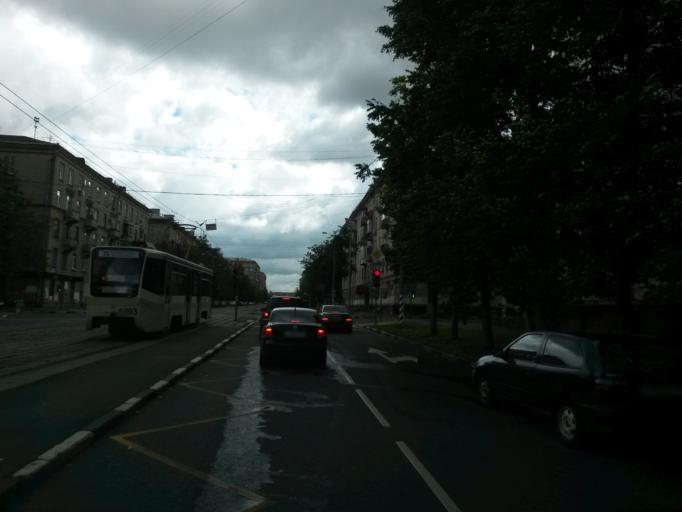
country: RU
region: Moskovskaya
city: Semenovskoye
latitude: 55.6839
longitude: 37.5589
